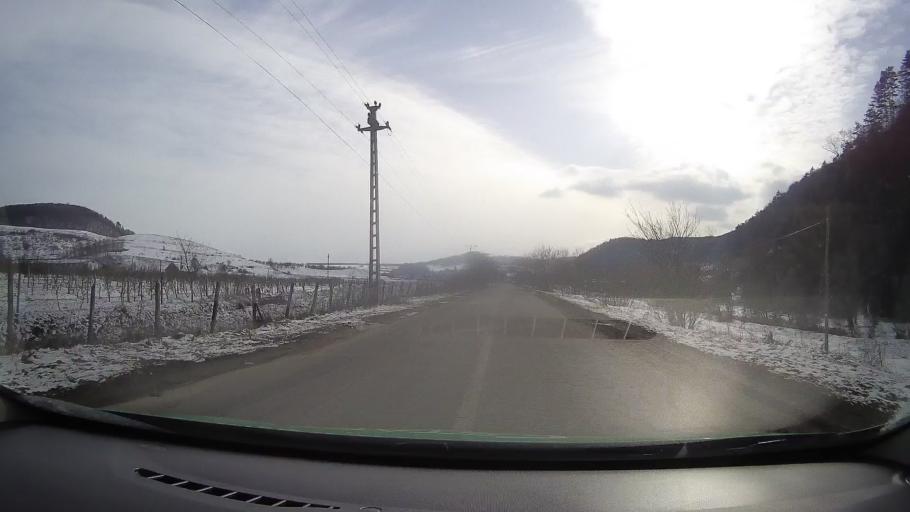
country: RO
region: Mures
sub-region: Comuna Apold
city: Apold
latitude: 46.1385
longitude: 24.8202
